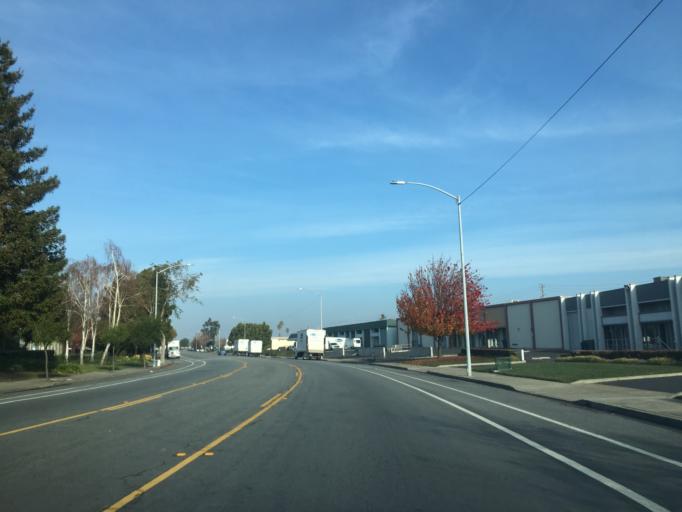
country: US
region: California
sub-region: Alameda County
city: San Leandro
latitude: 37.6945
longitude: -122.1633
